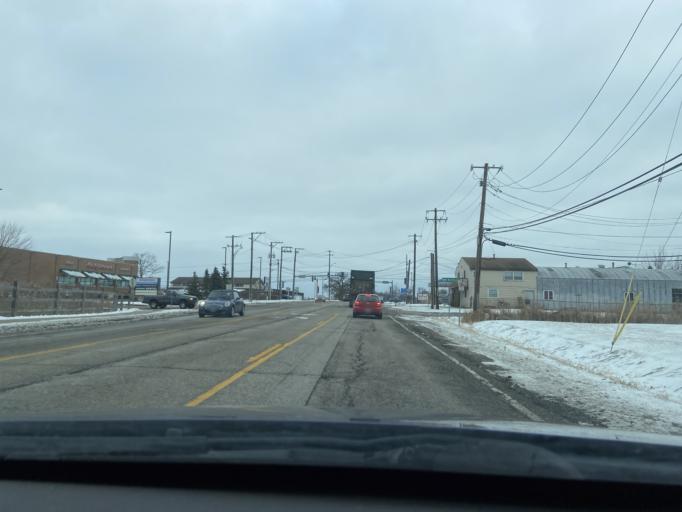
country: US
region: Illinois
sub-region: Lake County
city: Hainesville
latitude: 42.3463
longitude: -88.0676
